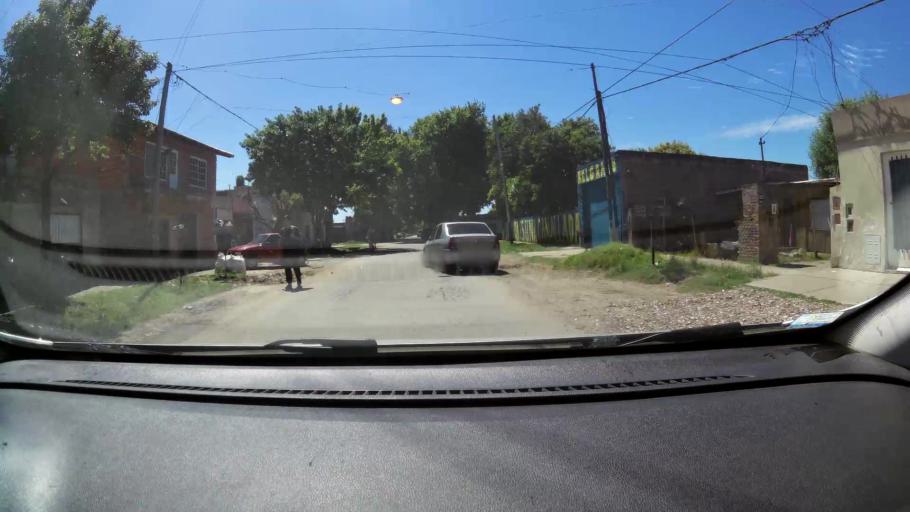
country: AR
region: Santa Fe
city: Perez
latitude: -32.9535
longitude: -60.7208
